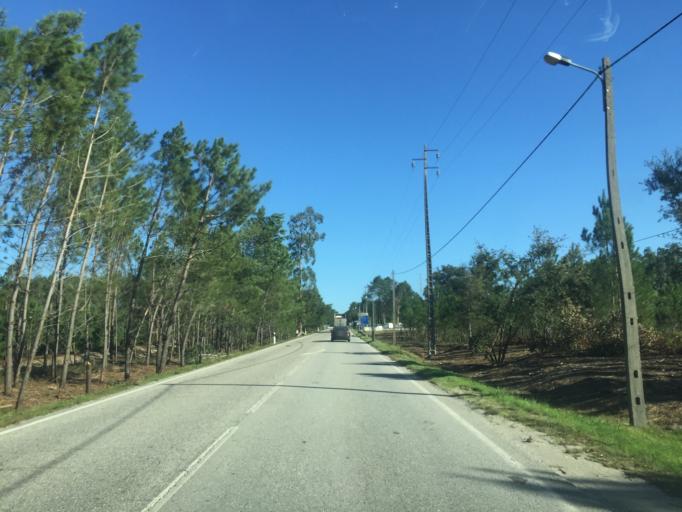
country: PT
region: Leiria
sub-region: Leiria
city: Monte Redondo
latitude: 39.9203
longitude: -8.8114
